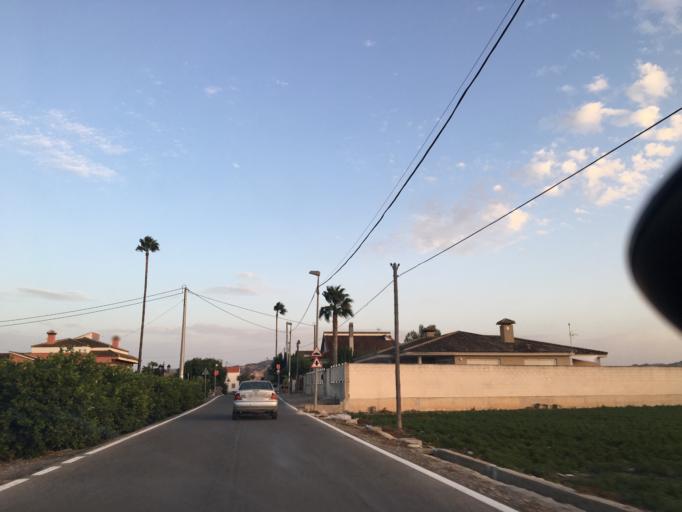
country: ES
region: Murcia
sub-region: Murcia
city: Santomera
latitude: 38.0318
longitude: -1.0604
